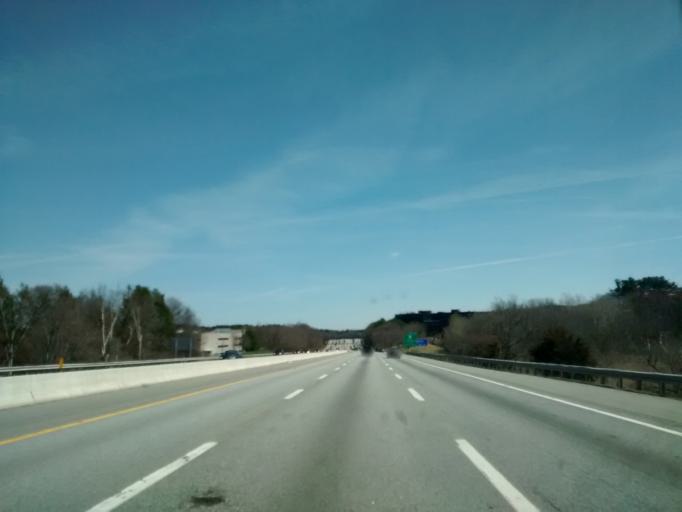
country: US
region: Massachusetts
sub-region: Middlesex County
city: Cochituate
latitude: 42.3151
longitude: -71.3992
